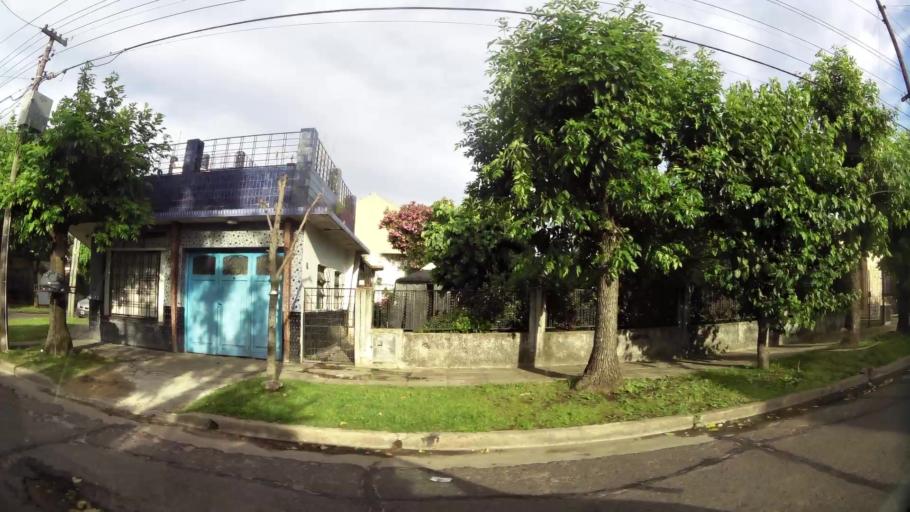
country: AR
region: Buenos Aires
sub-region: Partido de Moron
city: Moron
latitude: -34.6363
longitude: -58.6324
